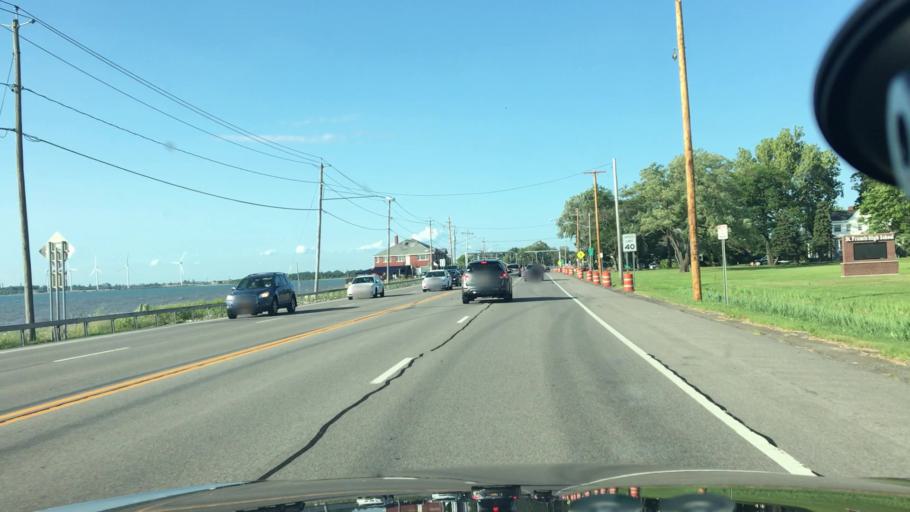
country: US
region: New York
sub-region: Erie County
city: Wanakah
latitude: 42.7715
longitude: -78.8654
